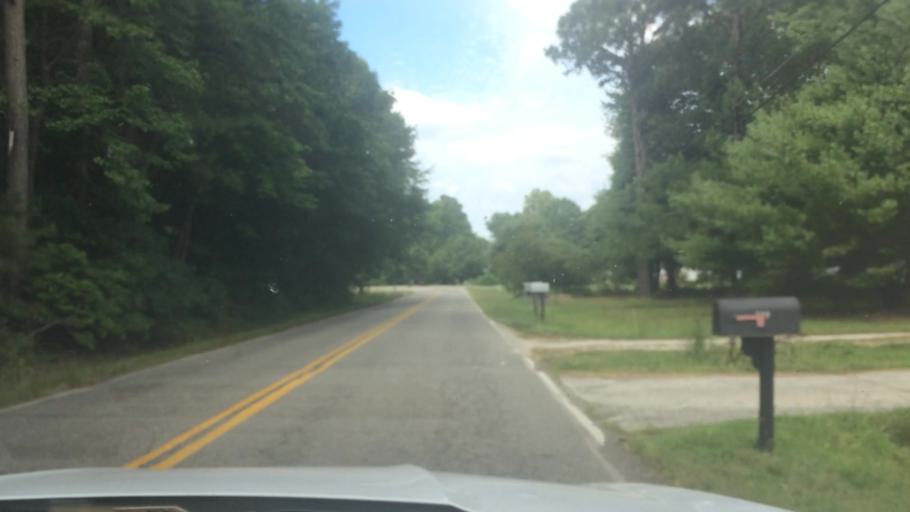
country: US
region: Virginia
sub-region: York County
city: Yorktown
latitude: 37.1746
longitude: -76.4348
